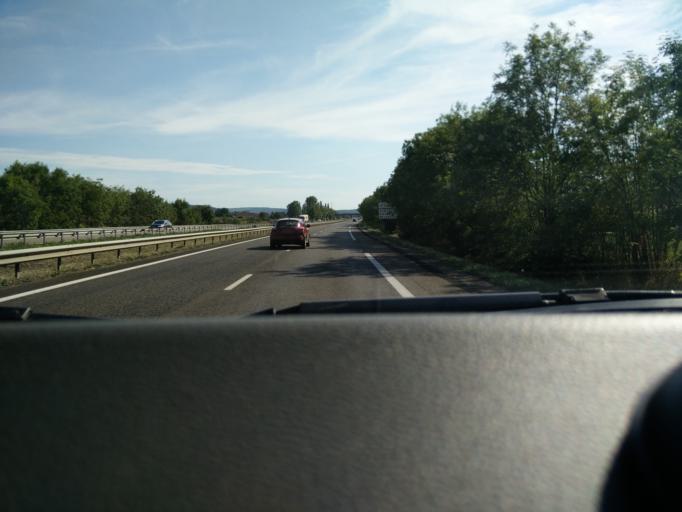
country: FR
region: Lorraine
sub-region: Departement de Meurthe-et-Moselle
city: Dieulouard
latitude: 48.8745
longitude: 6.0958
